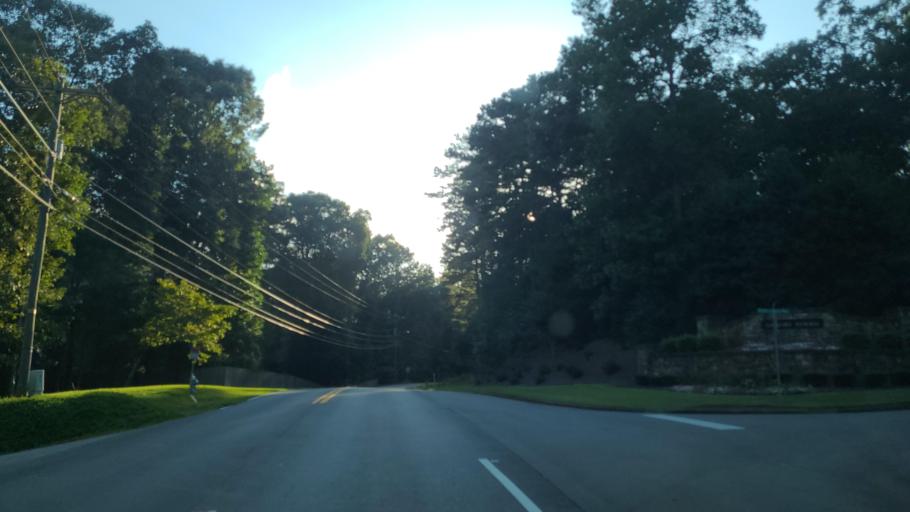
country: US
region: Georgia
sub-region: Fulton County
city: Milton
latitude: 34.1722
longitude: -84.3613
